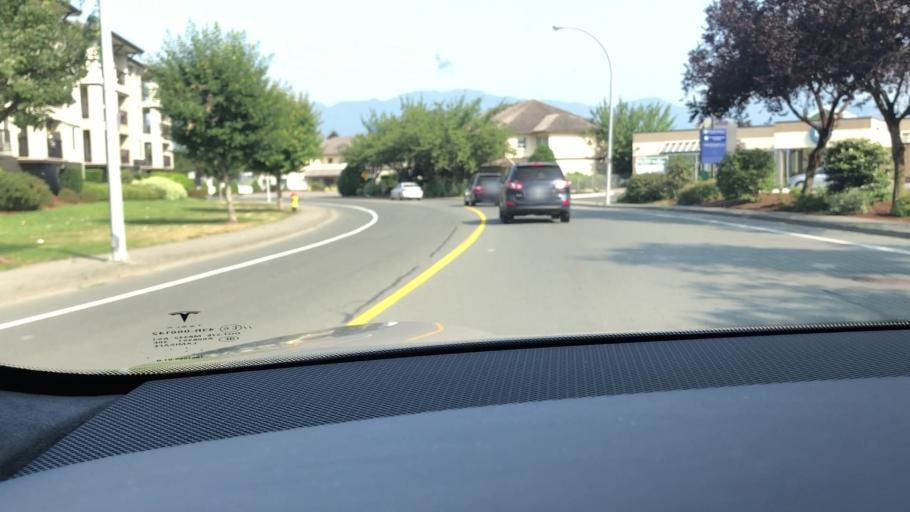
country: CA
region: British Columbia
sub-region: Fraser Valley Regional District
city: Chilliwack
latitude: 49.1389
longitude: -121.9647
